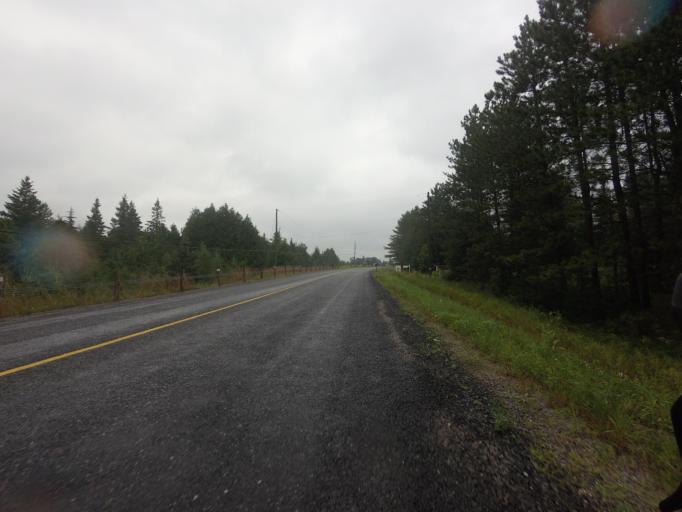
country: CA
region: Ontario
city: Perth
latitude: 45.0810
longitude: -76.4814
